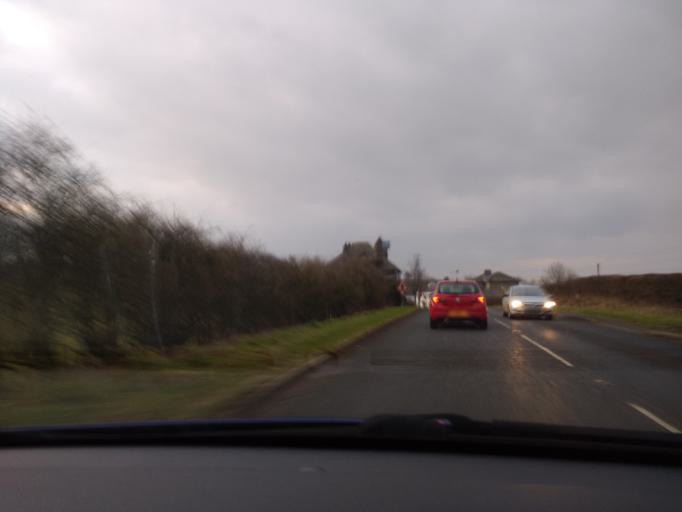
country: GB
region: England
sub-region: Cumbria
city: Kendal
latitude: 54.2885
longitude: -2.7291
